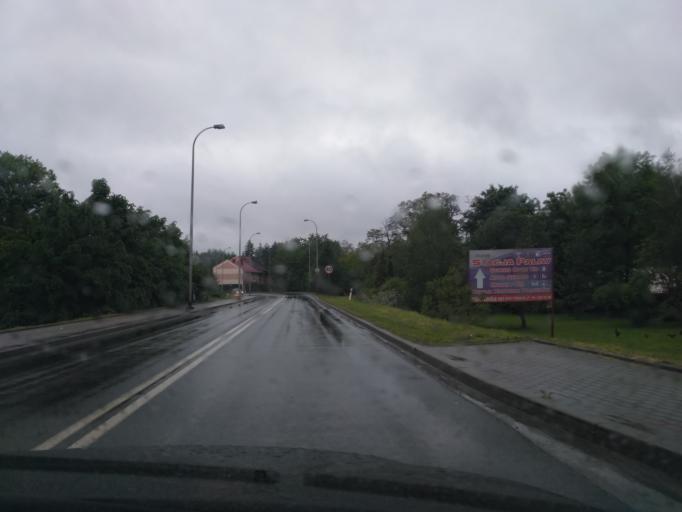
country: PL
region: Lesser Poland Voivodeship
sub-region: Powiat gorlicki
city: Gorlice
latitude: 49.6613
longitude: 21.1547
